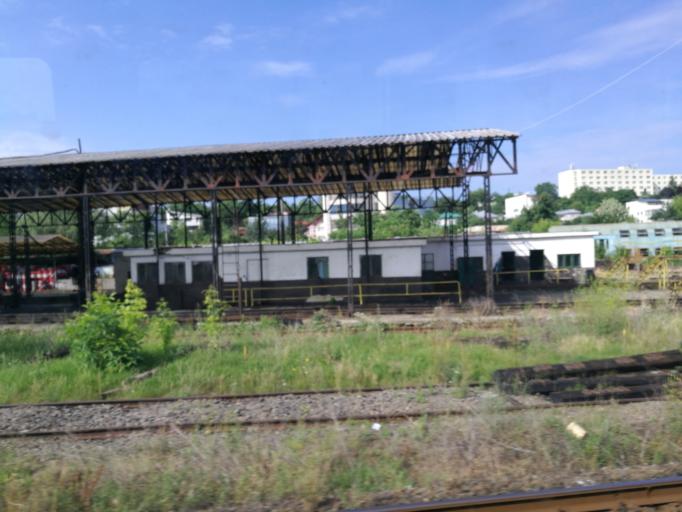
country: RO
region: Arges
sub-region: Comuna Bradu
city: Geamana
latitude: 44.8426
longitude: 24.8962
